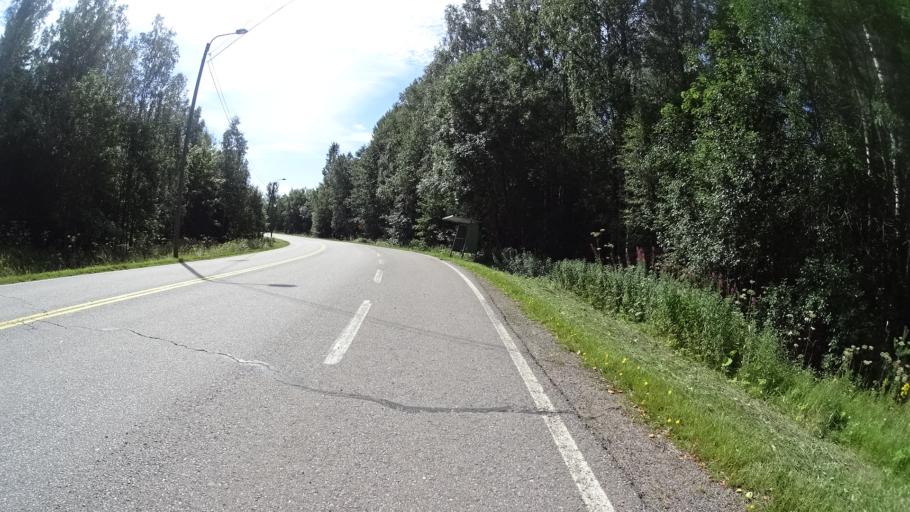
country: FI
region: Uusimaa
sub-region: Helsinki
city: Kirkkonummi
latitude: 60.1061
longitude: 24.4792
